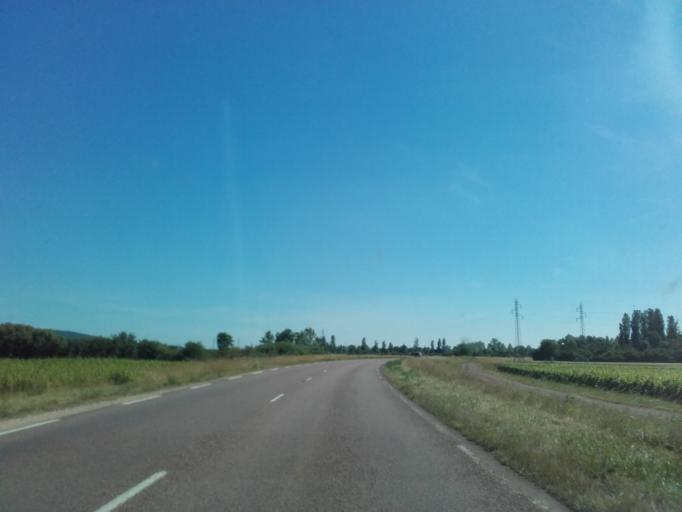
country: FR
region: Bourgogne
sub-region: Departement de Saone-et-Loire
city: Chagny
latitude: 46.9187
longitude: 4.7291
